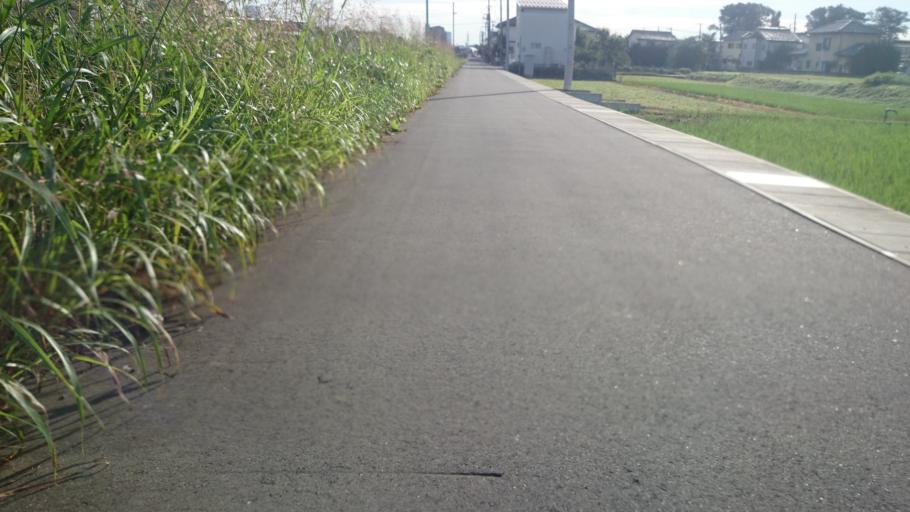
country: JP
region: Saitama
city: Yono
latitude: 35.8985
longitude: 139.5860
